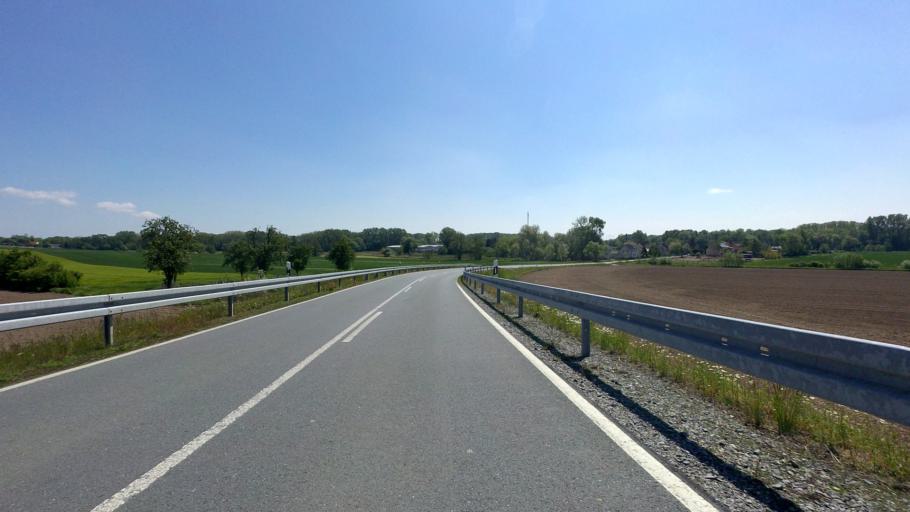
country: DE
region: Saxony
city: Stauchitz
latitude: 51.2736
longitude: 13.2503
